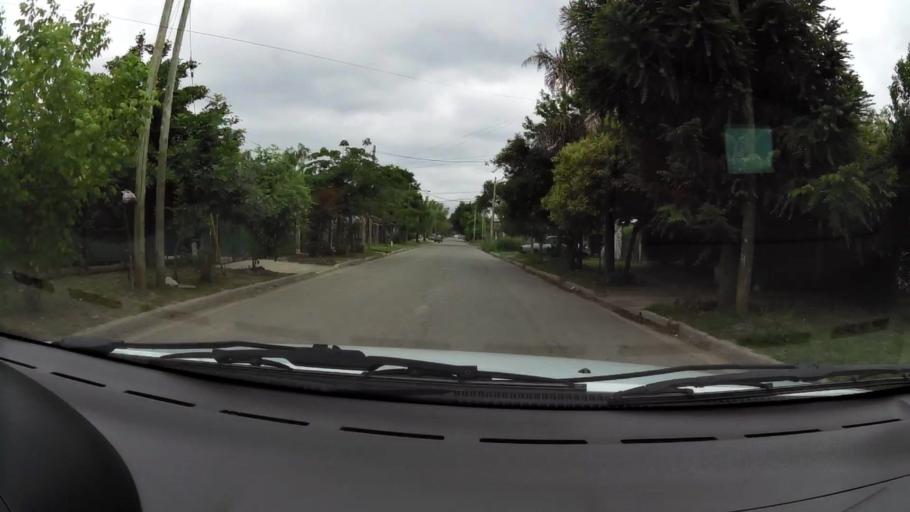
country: AR
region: Buenos Aires
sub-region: Partido de Ezeiza
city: Ezeiza
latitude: -34.8671
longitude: -58.5130
